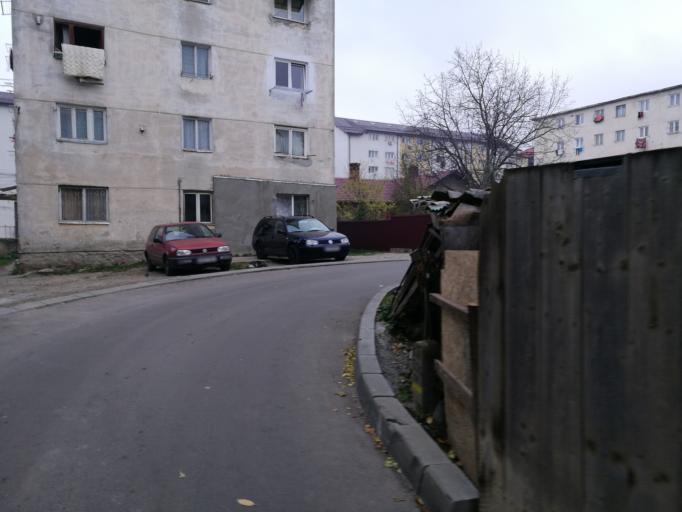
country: RO
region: Suceava
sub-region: Comuna Scheia
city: Scheia
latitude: 47.6716
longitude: 26.2682
